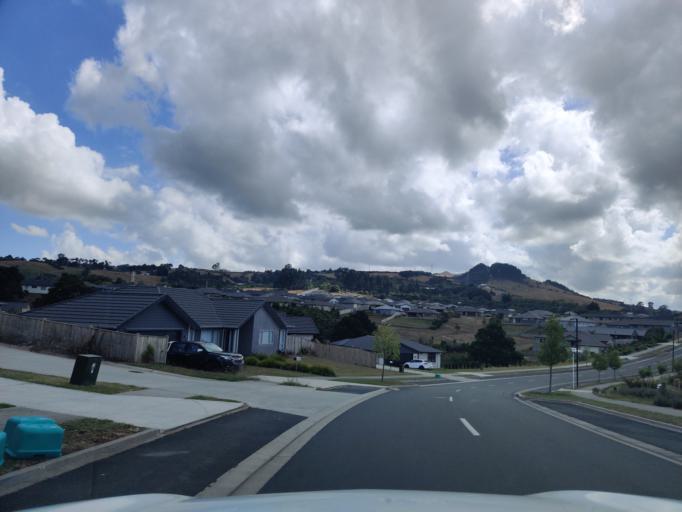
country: NZ
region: Auckland
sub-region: Auckland
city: Pukekohe East
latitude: -37.2349
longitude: 175.0102
